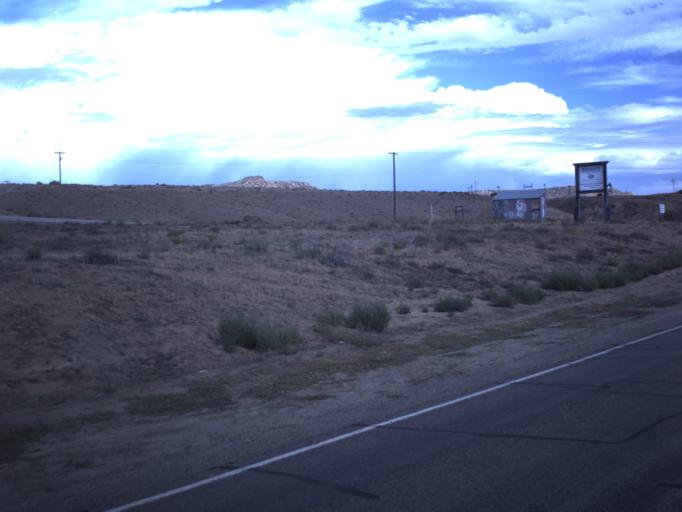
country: US
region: Utah
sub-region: San Juan County
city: Blanding
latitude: 37.2287
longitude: -109.2131
